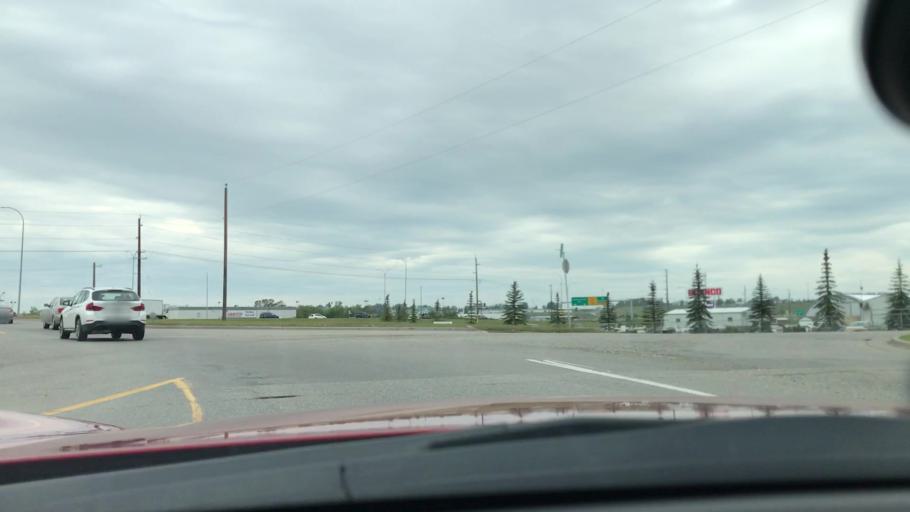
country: CA
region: Alberta
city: Calgary
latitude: 50.9898
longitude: -114.0254
